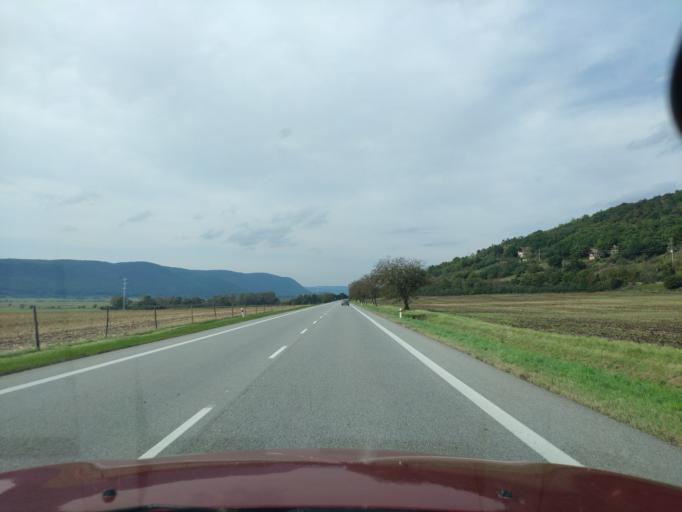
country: SK
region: Kosicky
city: Medzev
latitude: 48.6012
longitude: 20.8202
